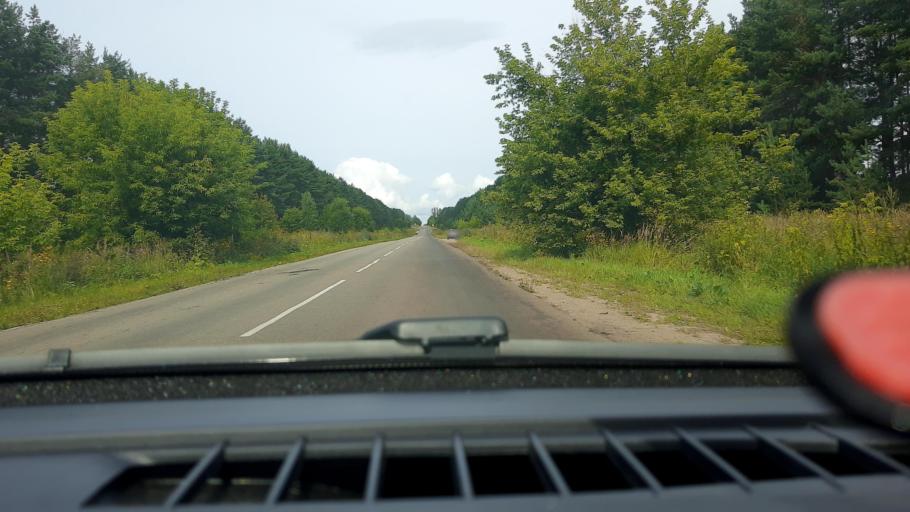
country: RU
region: Nizjnij Novgorod
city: Bogorodsk
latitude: 56.0841
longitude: 43.5691
